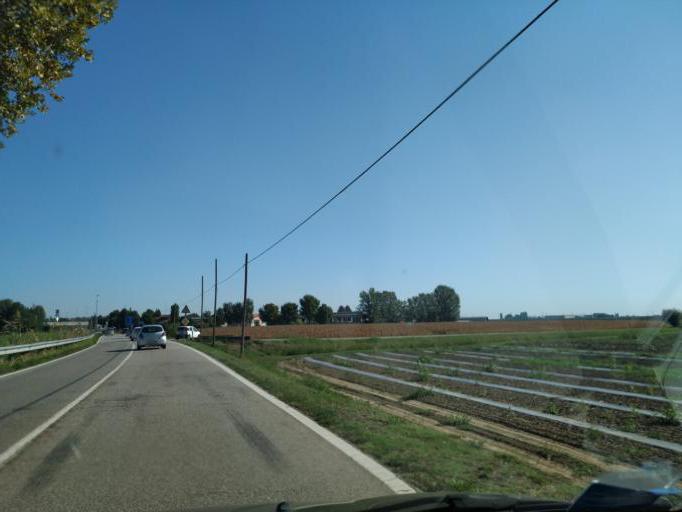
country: IT
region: Emilia-Romagna
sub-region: Provincia di Bologna
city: Decima
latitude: 44.6947
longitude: 11.2232
